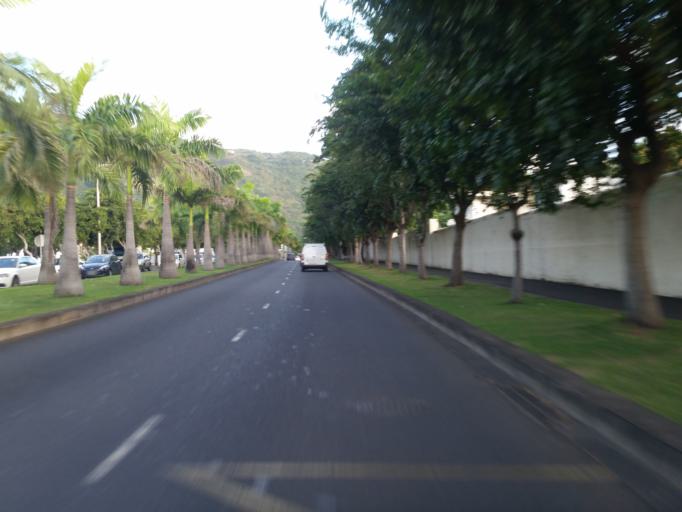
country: RE
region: Reunion
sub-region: Reunion
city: Saint-Denis
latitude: -20.8899
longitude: 55.4528
